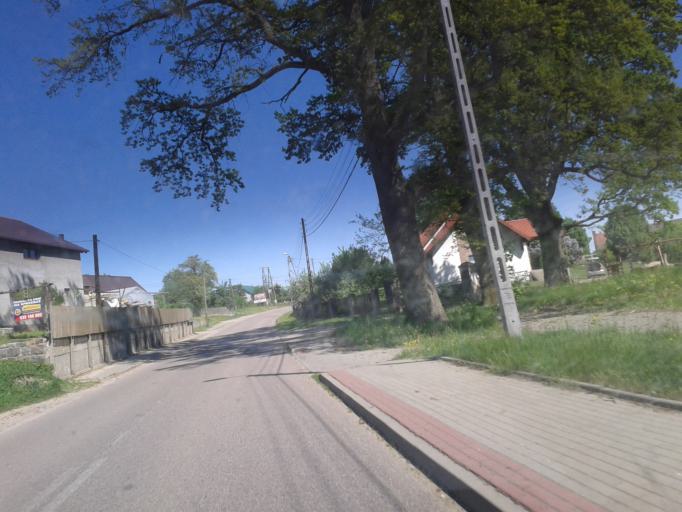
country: PL
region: West Pomeranian Voivodeship
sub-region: Powiat szczecinecki
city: Barwice
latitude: 53.7579
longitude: 16.2467
